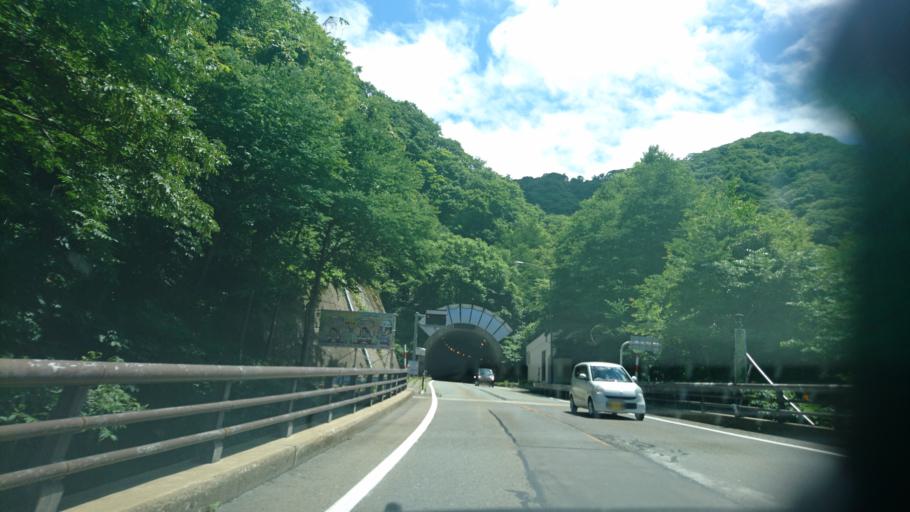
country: JP
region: Iwate
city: Shizukuishi
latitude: 39.6932
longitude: 140.7826
